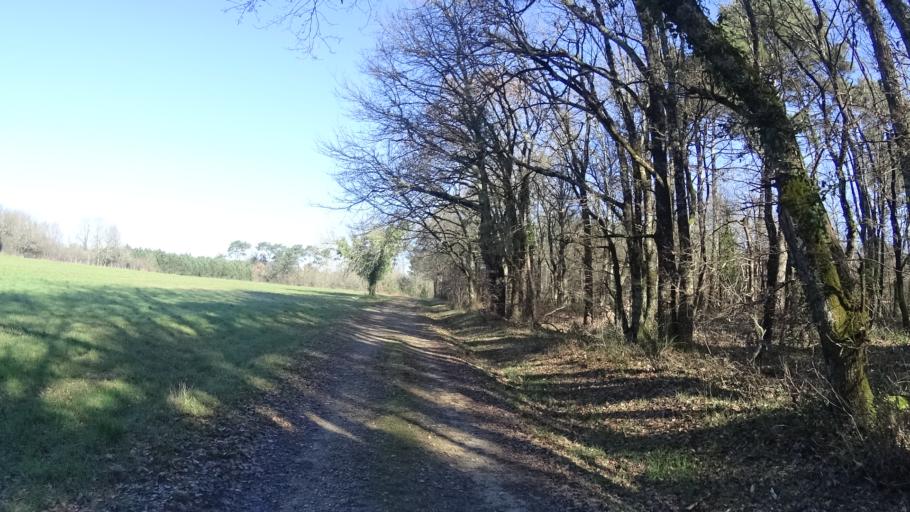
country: FR
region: Aquitaine
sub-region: Departement de la Dordogne
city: Saint-Medard-de-Mussidan
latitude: 45.0446
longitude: 0.2551
